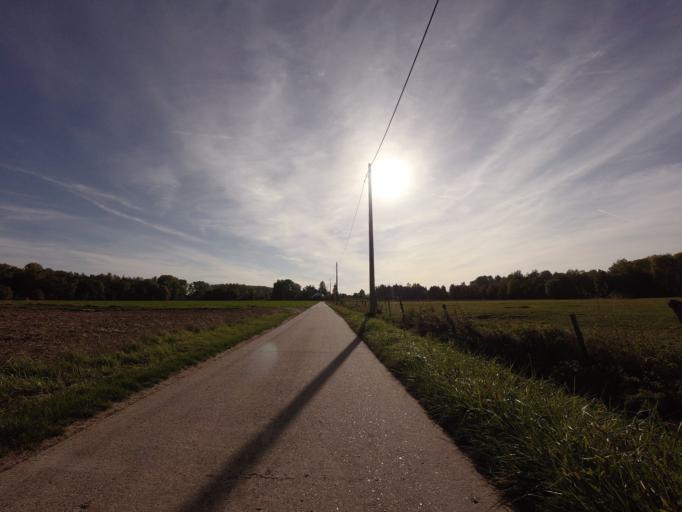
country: BE
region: Flanders
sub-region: Provincie Vlaams-Brabant
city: Kampenhout
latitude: 50.9126
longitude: 4.5966
